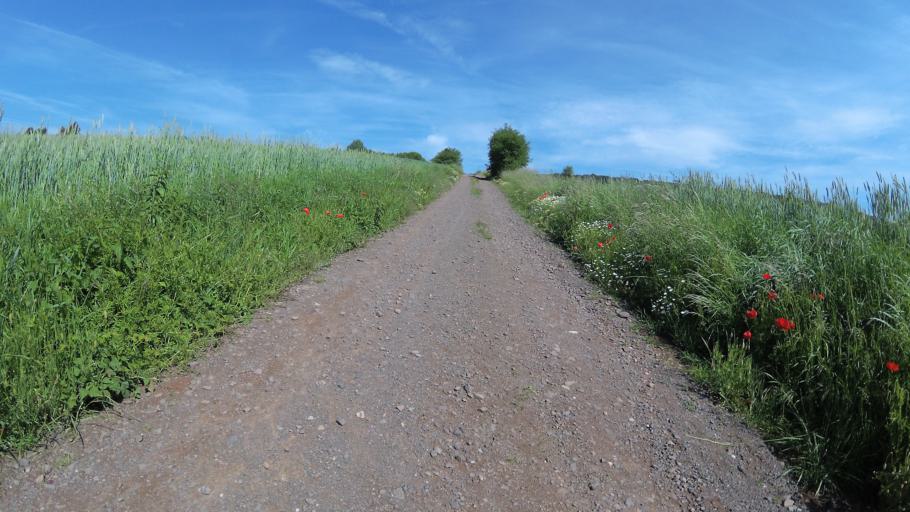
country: DE
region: Saarland
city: Ottweiler
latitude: 49.4321
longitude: 7.1718
